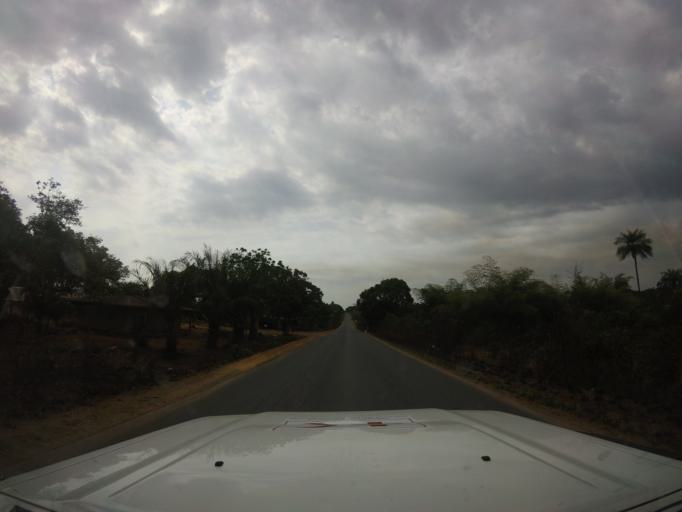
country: LR
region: Montserrado
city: Monrovia
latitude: 6.5470
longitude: -10.8609
